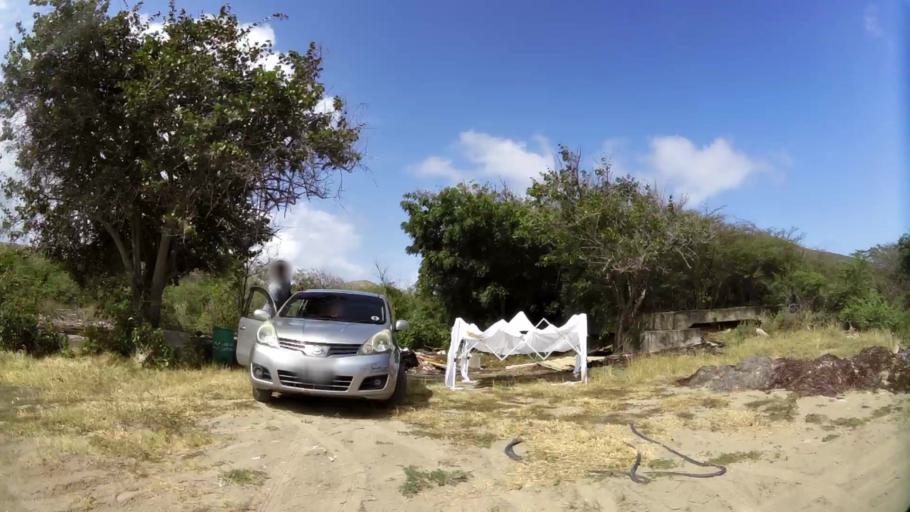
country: KN
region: Saint James Windwa
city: Newcastle
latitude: 17.2297
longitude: -62.6352
